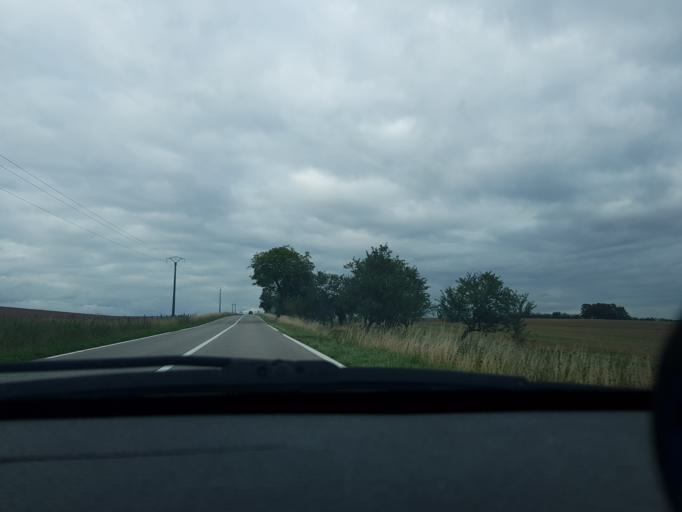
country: FR
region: Lorraine
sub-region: Departement de la Moselle
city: Chateau-Salins
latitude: 48.8641
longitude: 6.5270
